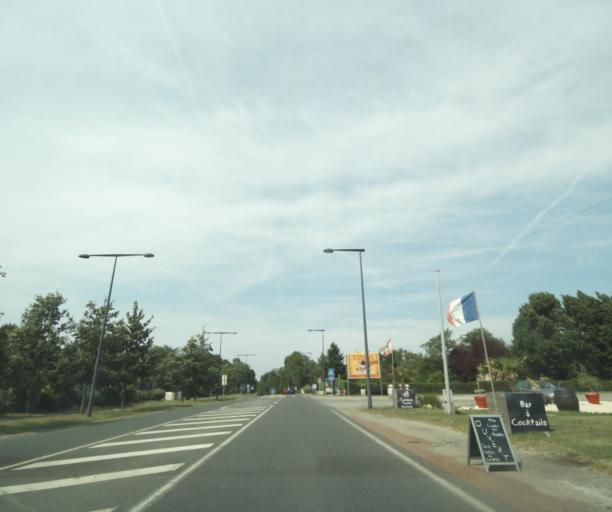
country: FR
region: Centre
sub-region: Departement d'Indre-et-Loire
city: Montbazon
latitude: 47.2785
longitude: 0.7107
